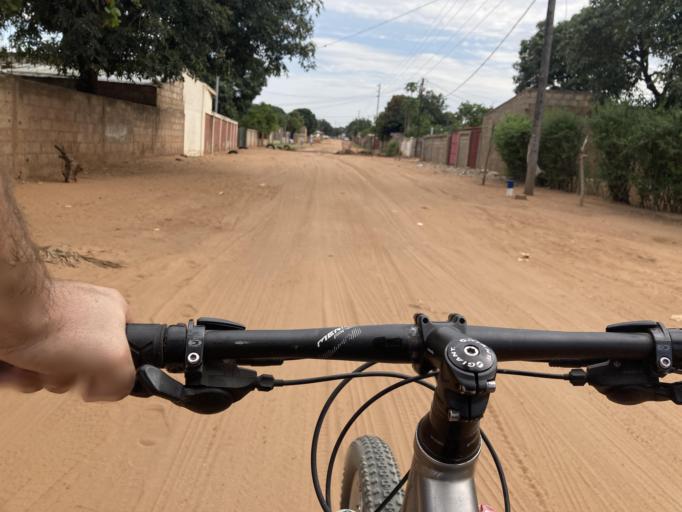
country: MZ
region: Maputo City
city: Maputo
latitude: -25.8931
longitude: 32.6079
